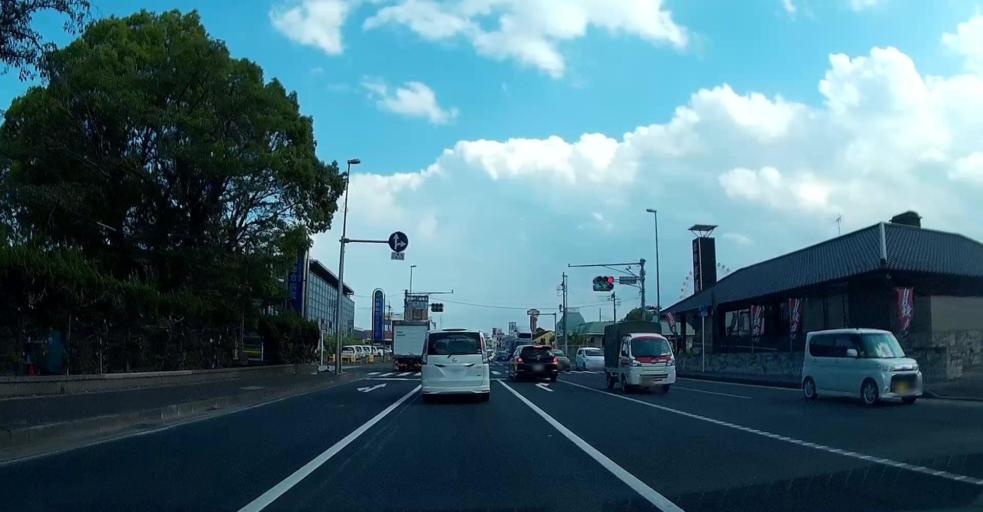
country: JP
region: Chiba
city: Noda
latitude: 35.9515
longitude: 139.8792
